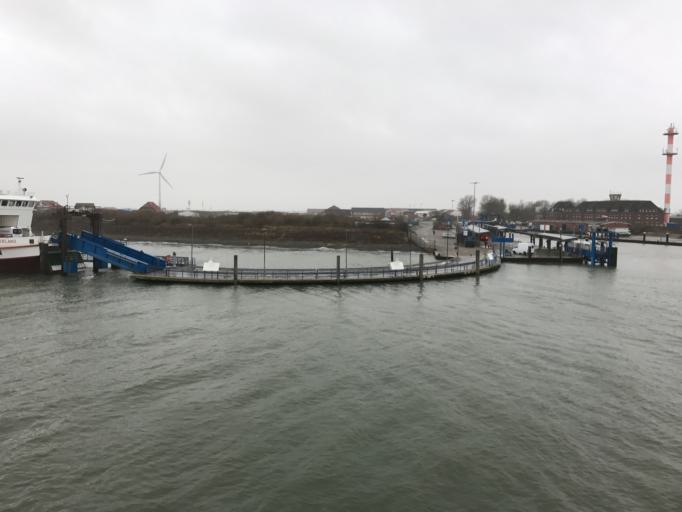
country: DE
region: Lower Saxony
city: Borkum
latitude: 53.5626
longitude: 6.7602
